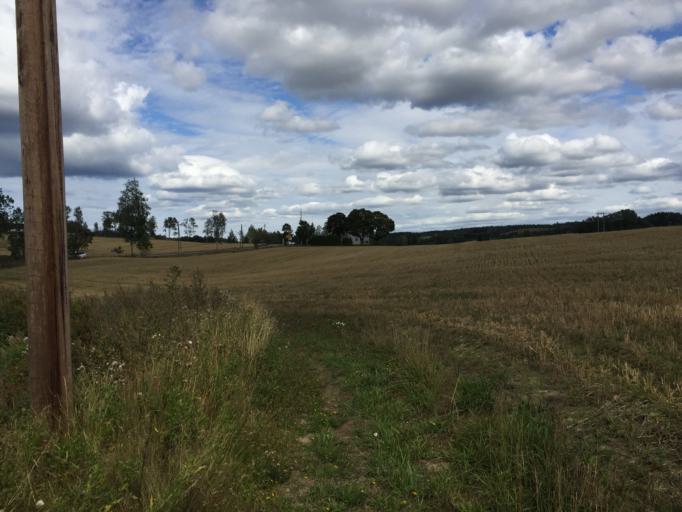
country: NO
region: Ostfold
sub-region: Hobol
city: Elvestad
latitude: 59.6179
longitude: 10.9437
